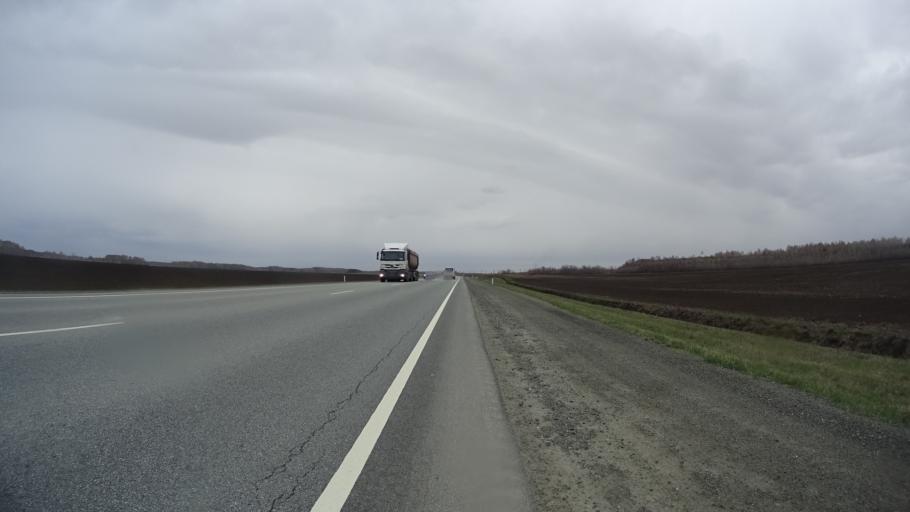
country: RU
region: Chelyabinsk
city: Krasnogorskiy
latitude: 54.5706
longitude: 61.2905
